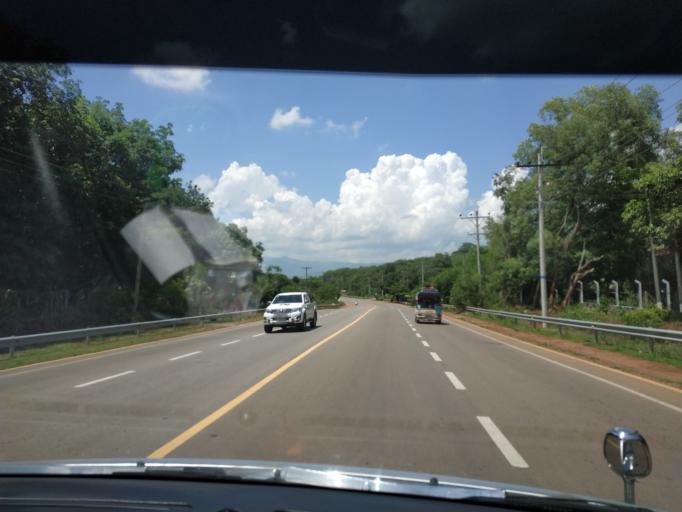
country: MM
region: Mon
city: Kyaikto
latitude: 17.3245
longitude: 97.0232
